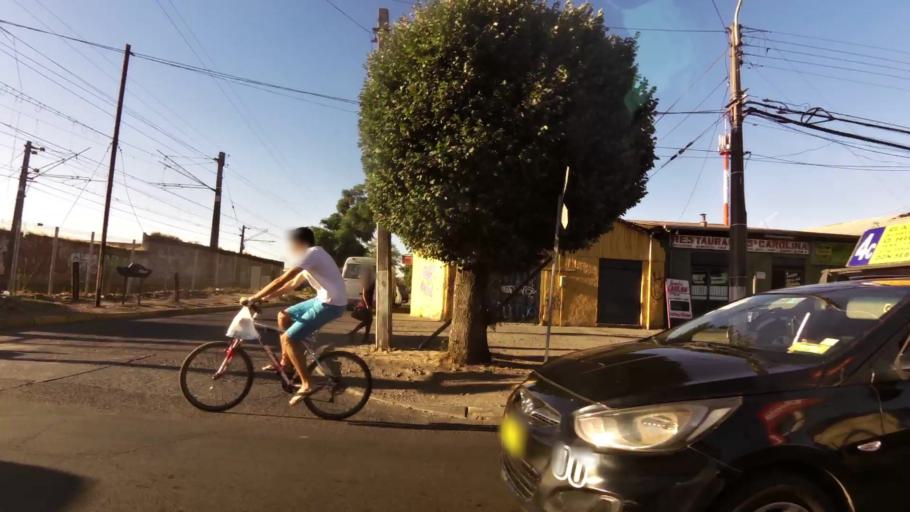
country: CL
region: Maule
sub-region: Provincia de Curico
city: Curico
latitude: -34.9817
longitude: -71.2465
